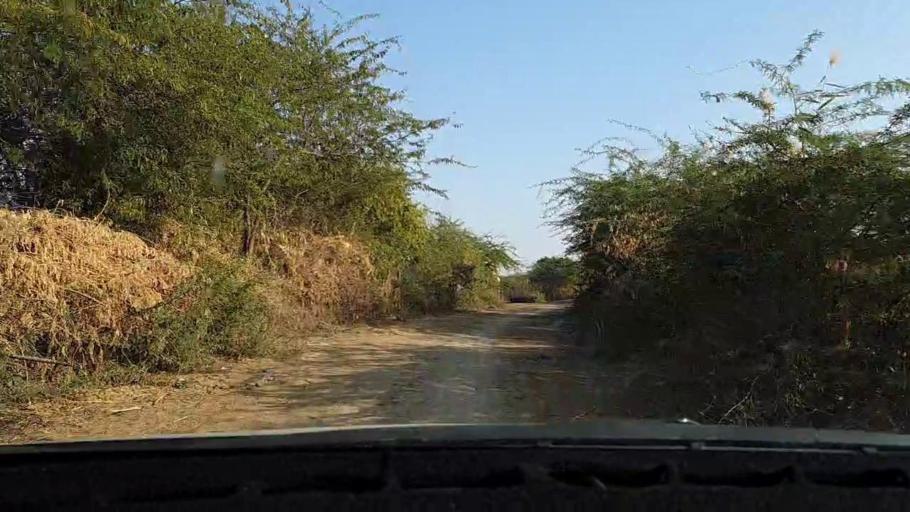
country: PK
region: Sindh
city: Tando Mittha Khan
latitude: 25.8336
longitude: 69.3191
